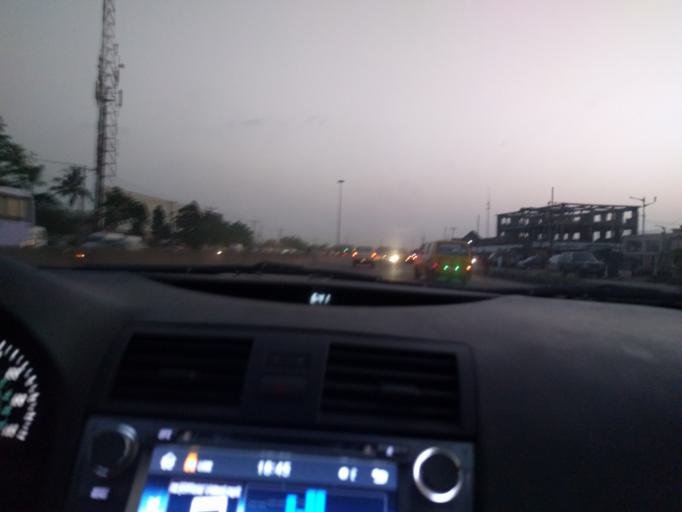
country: NG
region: Lagos
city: Mushin
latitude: 6.5210
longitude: 3.3351
